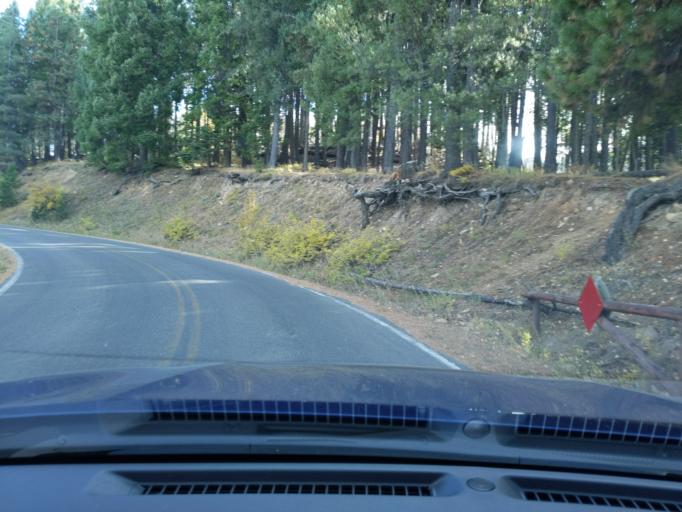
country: US
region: Arizona
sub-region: Pima County
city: Catalina
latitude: 32.4521
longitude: -110.7837
